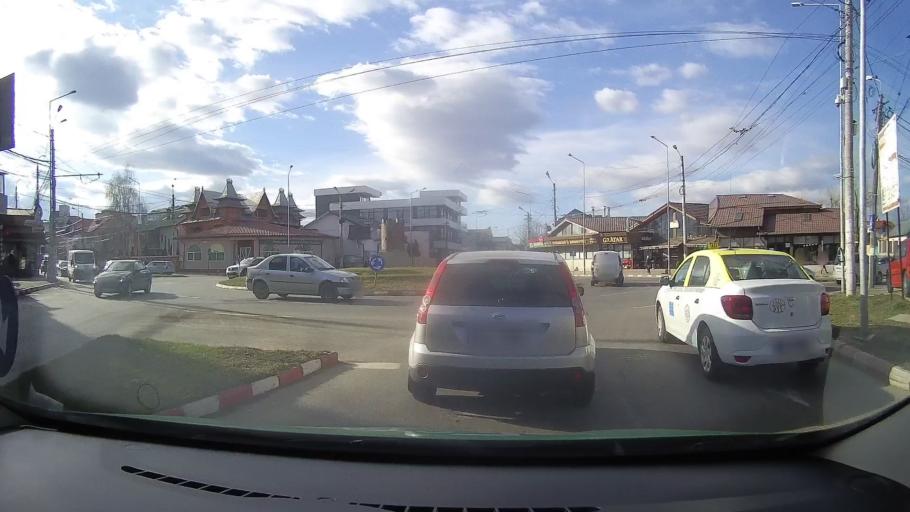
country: RO
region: Dambovita
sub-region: Comuna Lucieni
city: Lucieni
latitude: 44.8592
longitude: 25.4177
